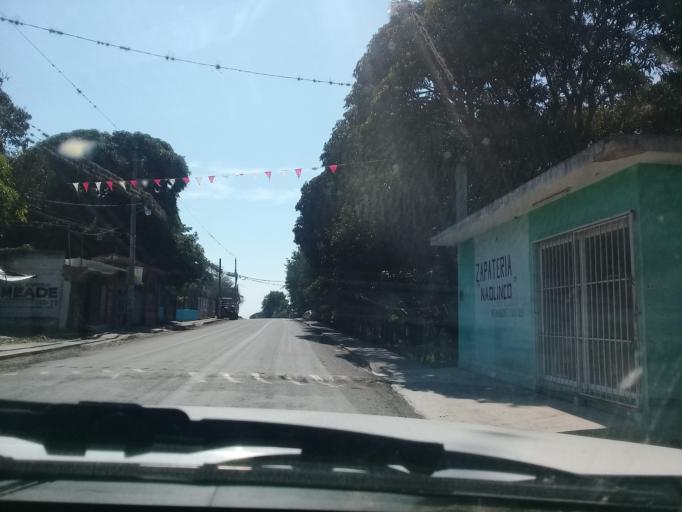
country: MX
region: Veracruz
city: Actopan
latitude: 19.4717
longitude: -96.5777
